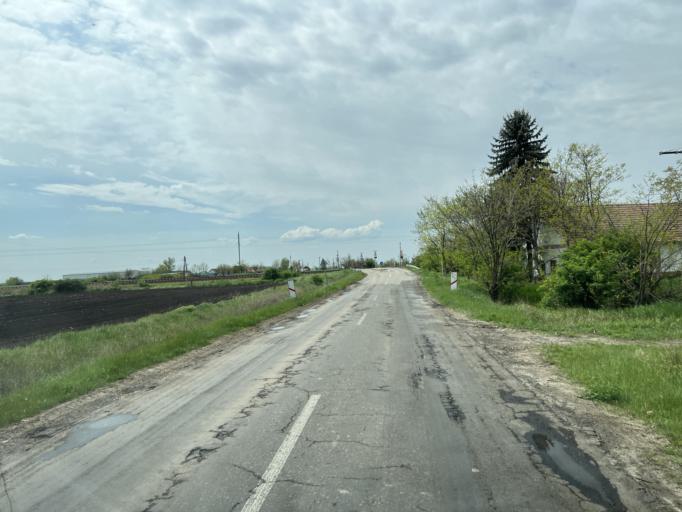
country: HU
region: Pest
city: Abony
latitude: 47.1752
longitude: 19.9892
